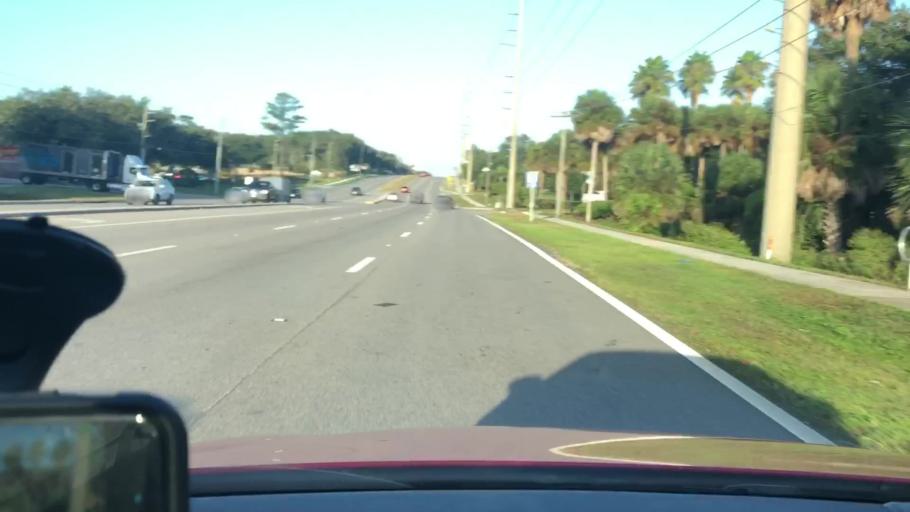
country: US
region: Florida
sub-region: Volusia County
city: Deltona
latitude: 28.9114
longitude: -81.2831
